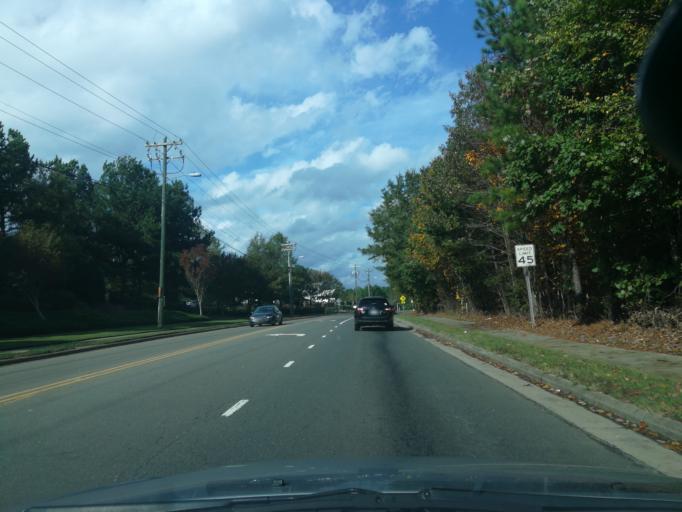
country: US
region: North Carolina
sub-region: Durham County
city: Durham
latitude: 36.0472
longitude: -78.9362
